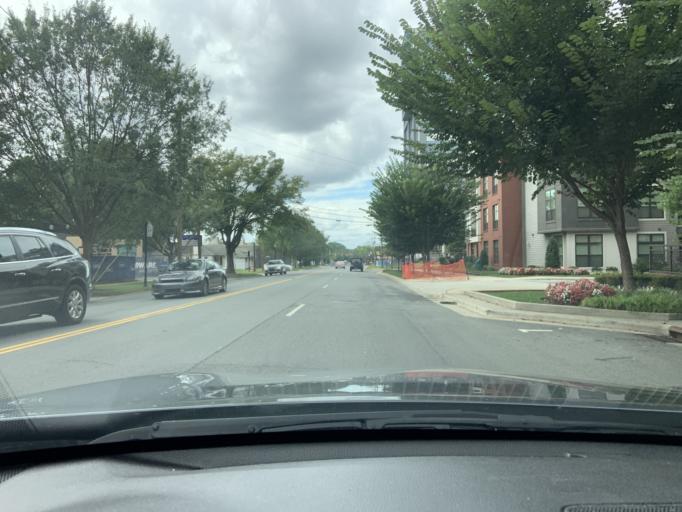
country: US
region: North Carolina
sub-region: Mecklenburg County
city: Charlotte
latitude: 35.2129
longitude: -80.8593
